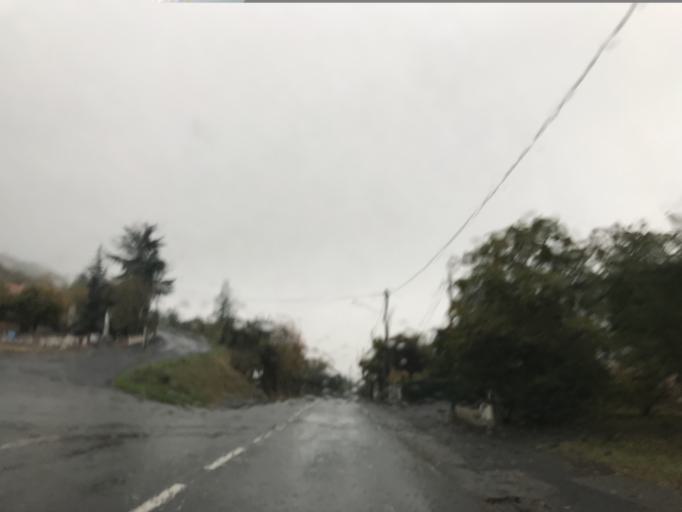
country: FR
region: Auvergne
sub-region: Departement du Puy-de-Dome
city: Durtol
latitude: 45.7970
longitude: 3.0590
